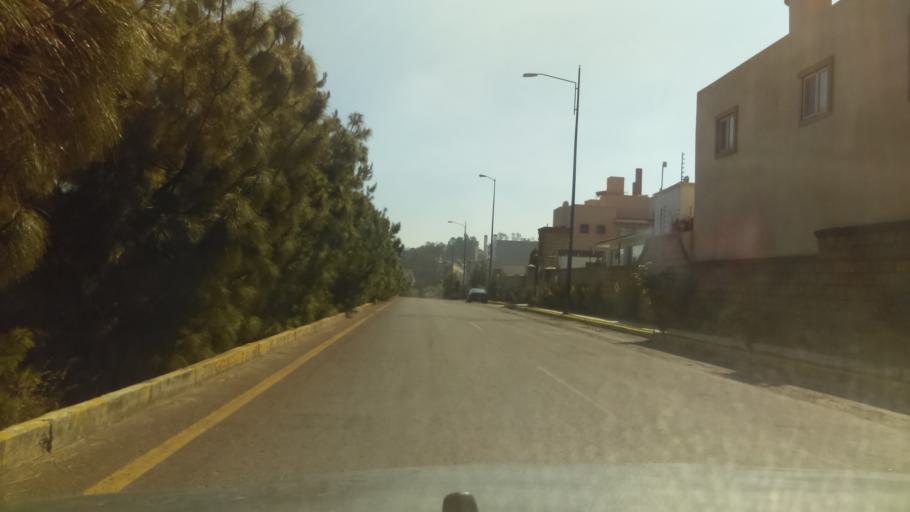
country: MX
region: Michoacan
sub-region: Morelia
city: Montana Monarca (Punta Altozano)
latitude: 19.6582
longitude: -101.1703
